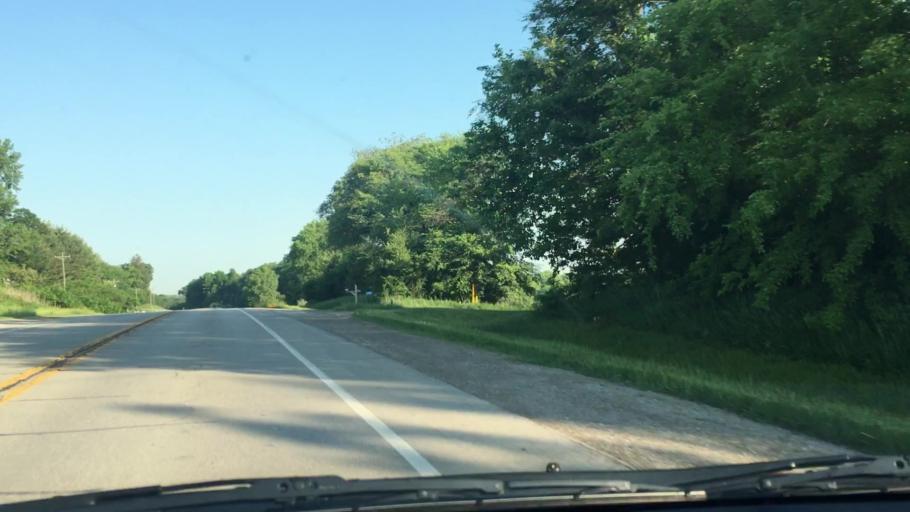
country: US
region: Iowa
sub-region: Johnson County
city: Tiffin
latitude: 41.7096
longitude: -91.6881
